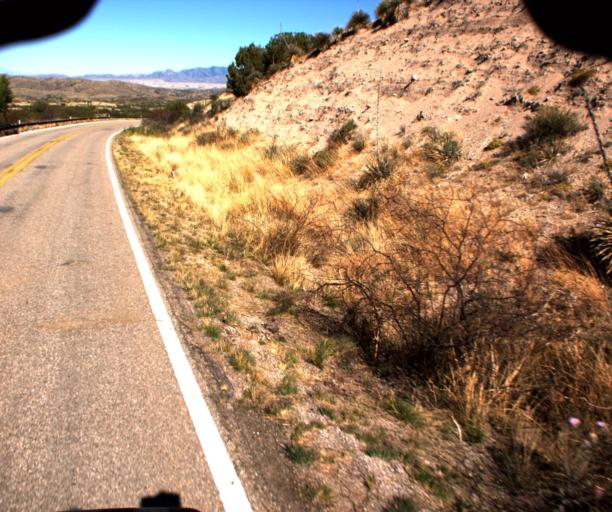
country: US
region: Arizona
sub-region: Pima County
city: Corona de Tucson
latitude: 31.8311
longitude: -110.7113
